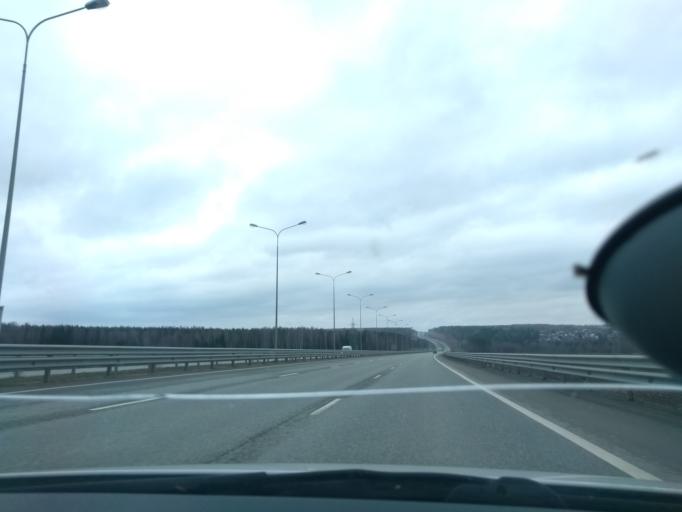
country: RU
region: Perm
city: Bershet'
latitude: 57.7110
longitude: 56.3634
